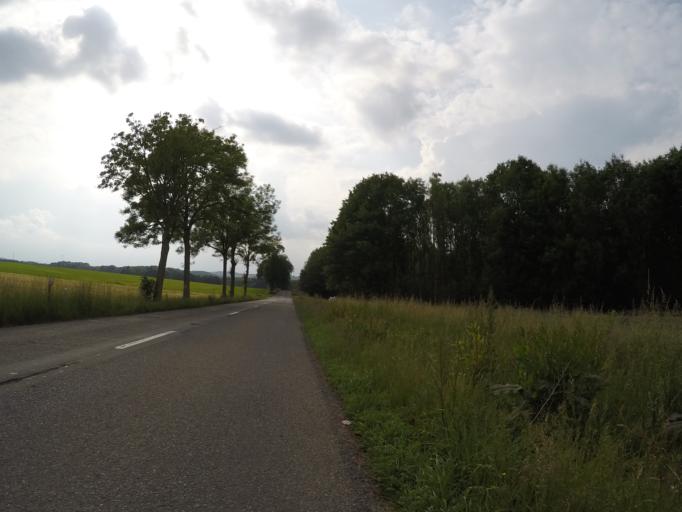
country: BE
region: Wallonia
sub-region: Province de Namur
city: Assesse
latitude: 50.3140
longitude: 5.0390
